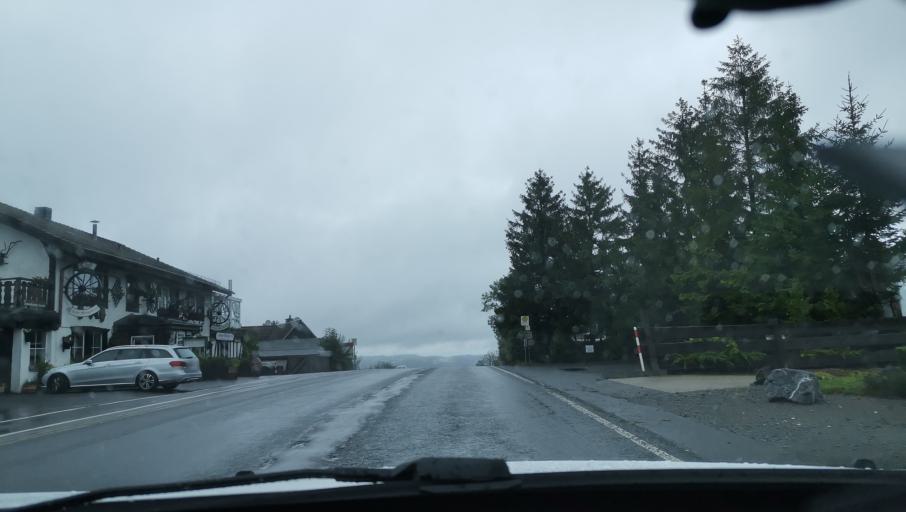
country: DE
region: North Rhine-Westphalia
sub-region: Regierungsbezirk Arnsberg
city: Breckerfeld
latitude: 51.2475
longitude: 7.4654
